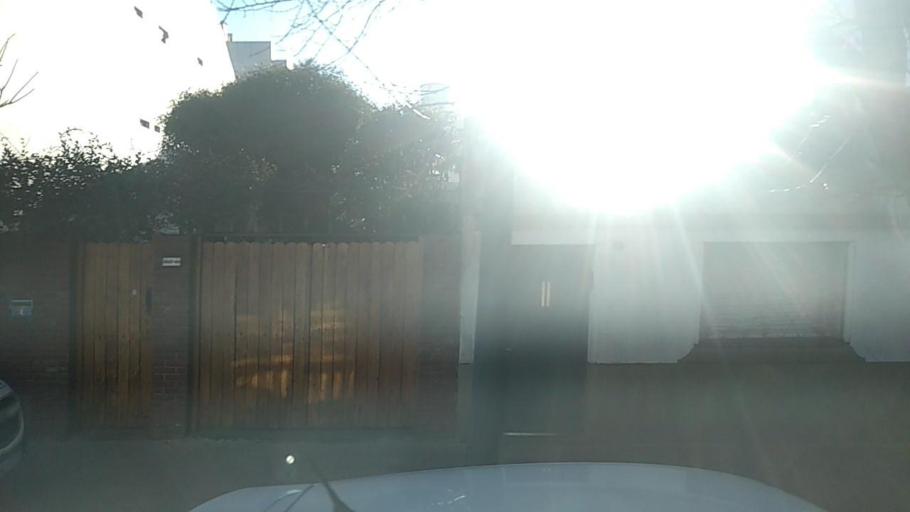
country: AR
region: Buenos Aires F.D.
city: Villa Santa Rita
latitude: -34.6240
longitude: -58.5062
